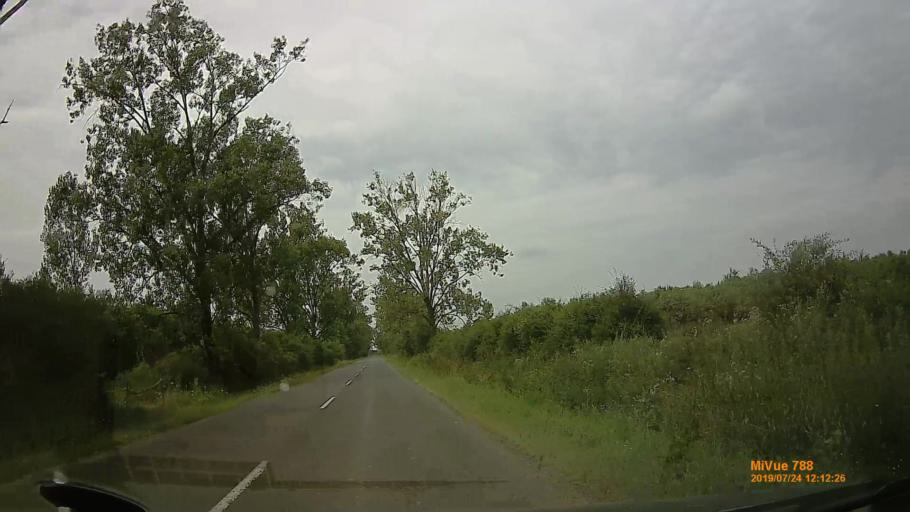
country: HU
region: Szabolcs-Szatmar-Bereg
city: Vasarosnameny
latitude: 48.1956
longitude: 22.3820
